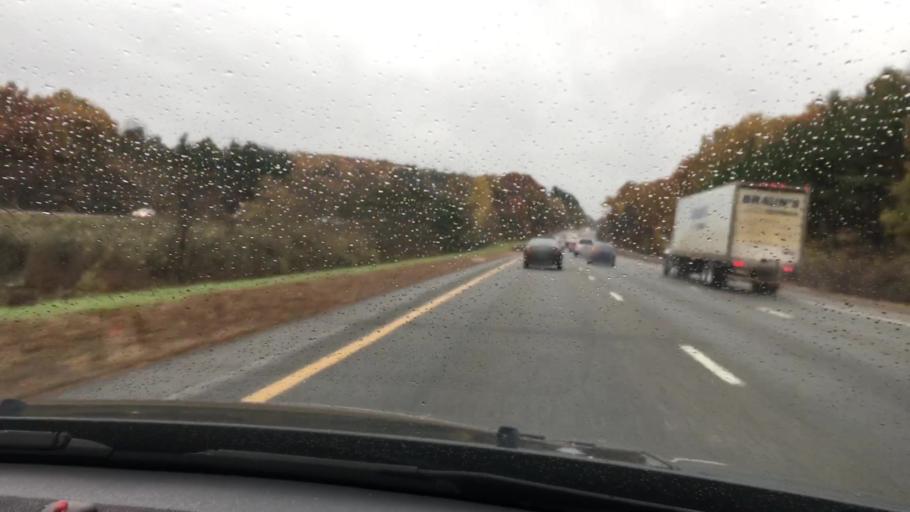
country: US
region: Massachusetts
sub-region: Worcester County
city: Harvard
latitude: 42.4746
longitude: -71.5548
